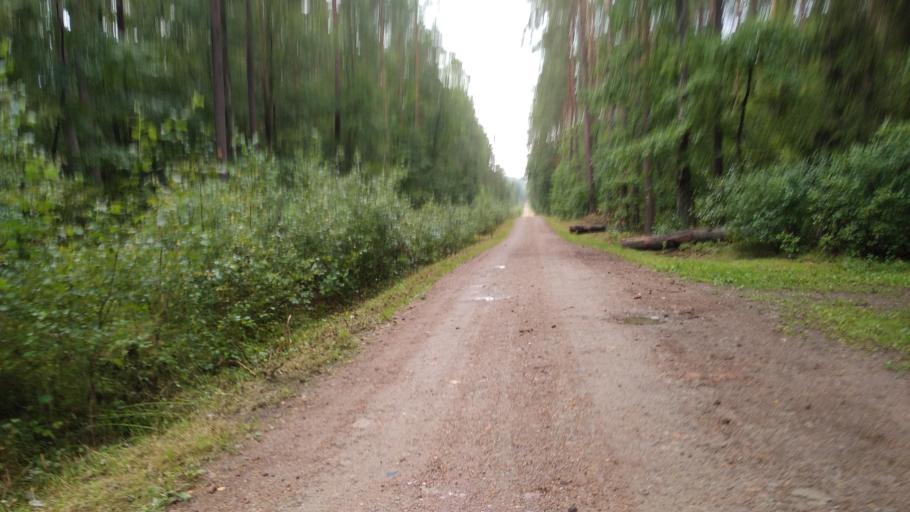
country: PL
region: Pomeranian Voivodeship
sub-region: Powiat wejherowski
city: Goscicino
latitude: 54.6188
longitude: 18.1558
